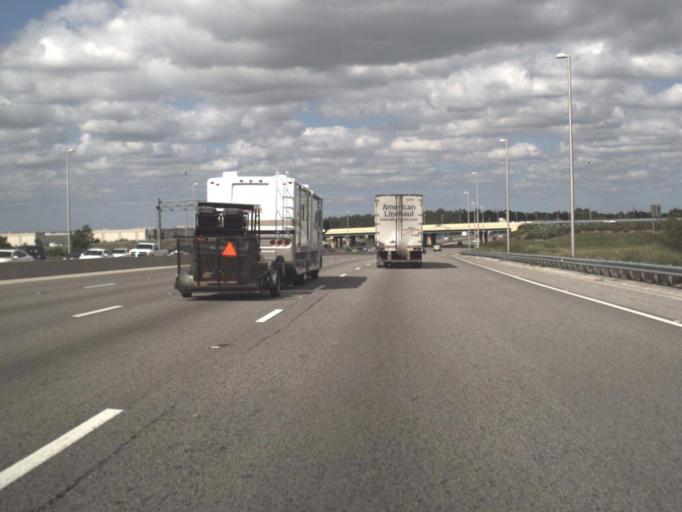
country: US
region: Florida
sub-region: Orange County
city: Sky Lake
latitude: 28.4311
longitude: -81.4058
